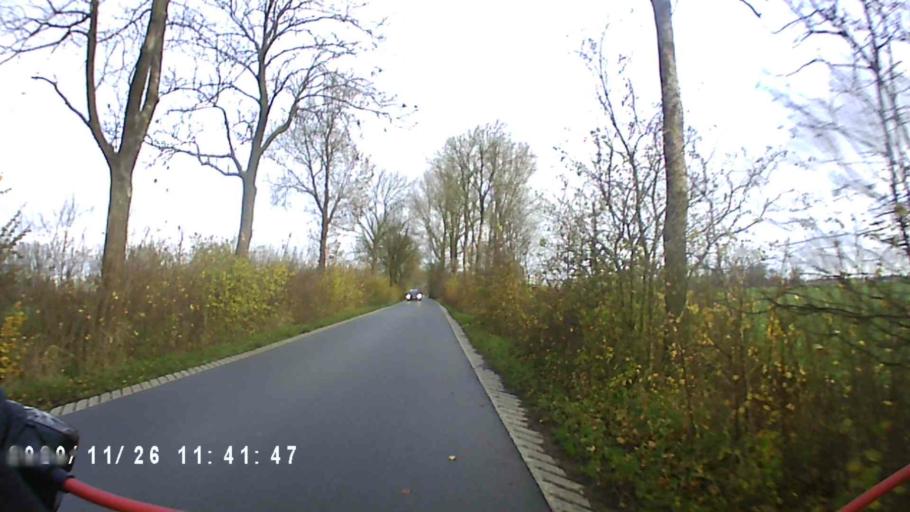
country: NL
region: Groningen
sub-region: Gemeente Bedum
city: Bedum
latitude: 53.2923
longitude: 6.5724
